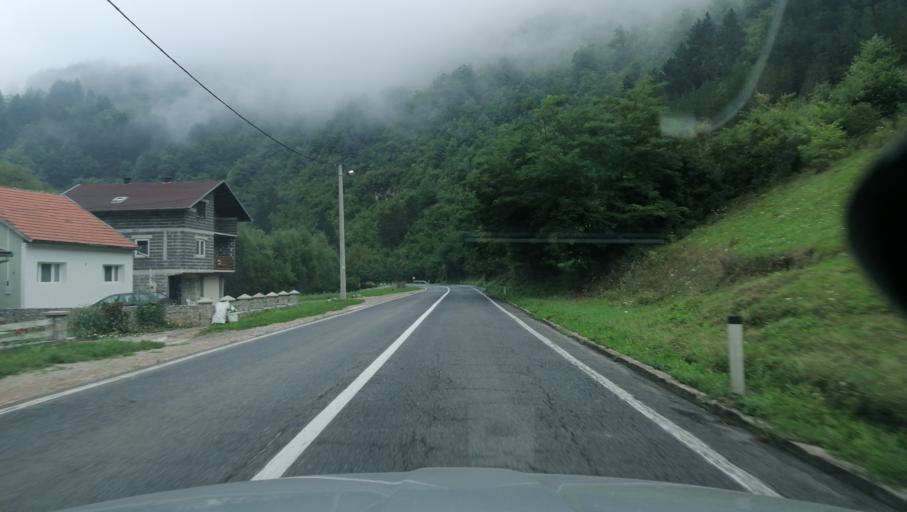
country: BA
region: Federation of Bosnia and Herzegovina
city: Donji Vakuf
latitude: 44.1504
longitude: 17.3765
